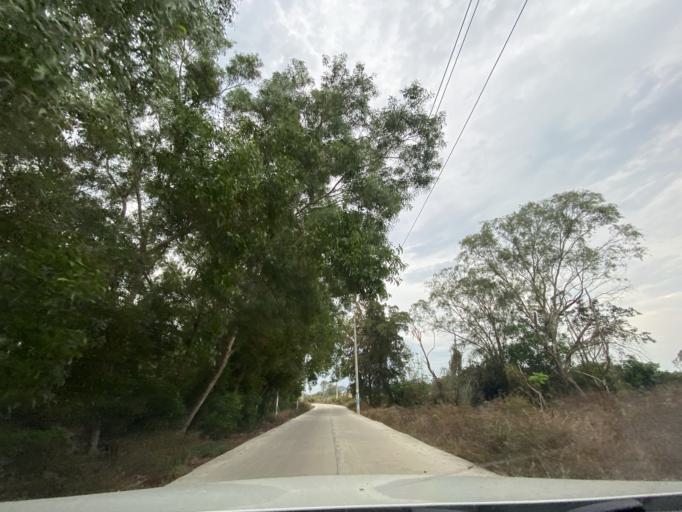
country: CN
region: Hainan
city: Yingzhou
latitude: 18.4092
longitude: 109.8206
